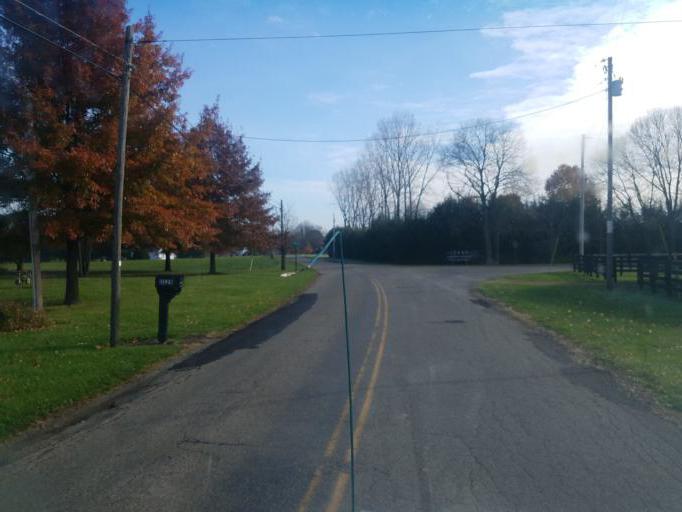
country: US
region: Ohio
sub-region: Knox County
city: Fredericktown
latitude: 40.4243
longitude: -82.5351
